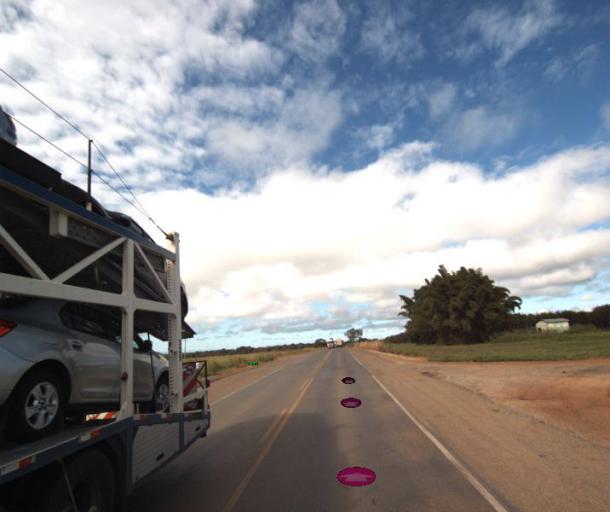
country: BR
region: Goias
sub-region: Uruacu
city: Uruacu
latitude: -14.7505
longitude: -49.2532
